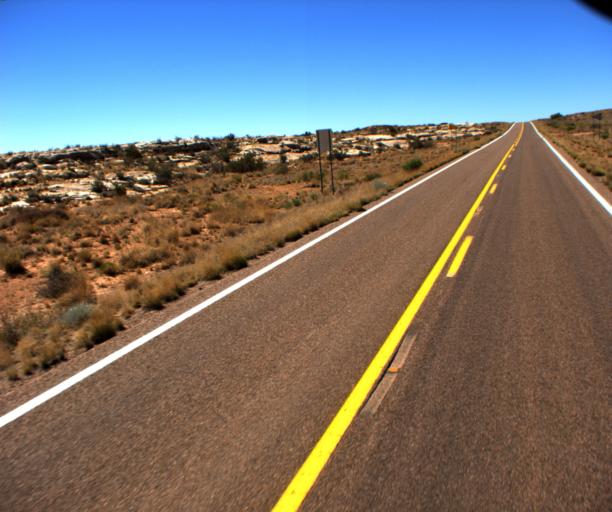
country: US
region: Arizona
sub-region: Navajo County
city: Winslow
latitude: 34.9640
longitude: -110.6470
